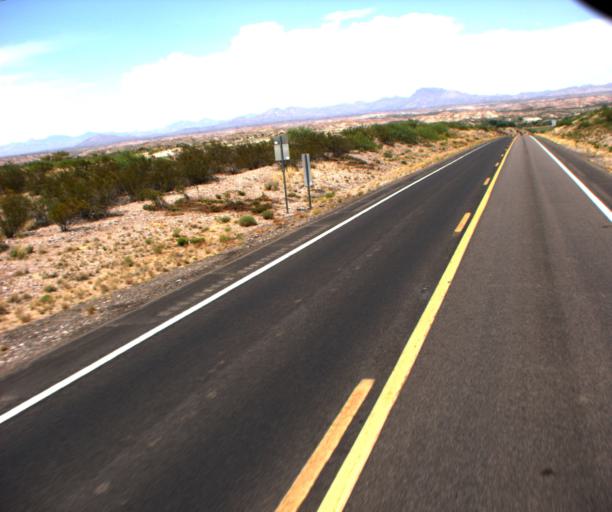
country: US
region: Arizona
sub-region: Greenlee County
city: Clifton
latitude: 32.7378
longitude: -109.1433
